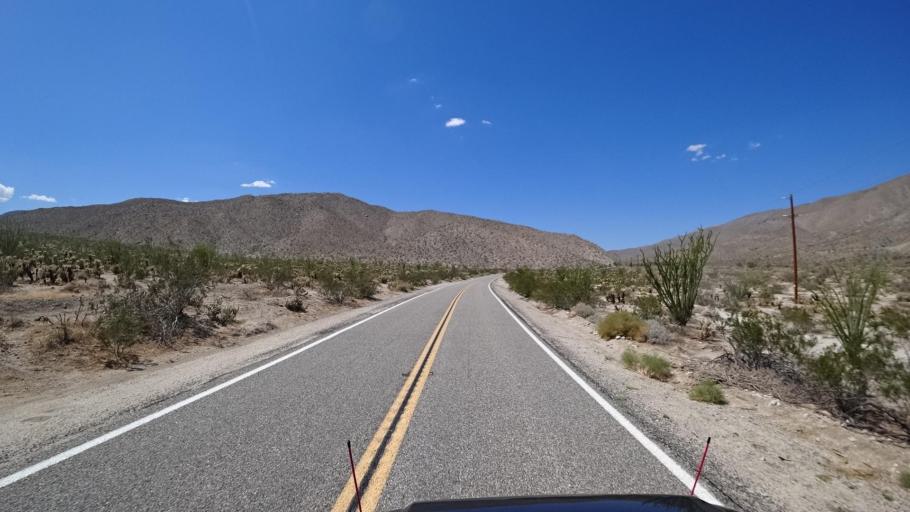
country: US
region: California
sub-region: San Diego County
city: Borrego Springs
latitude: 33.1341
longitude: -116.3622
